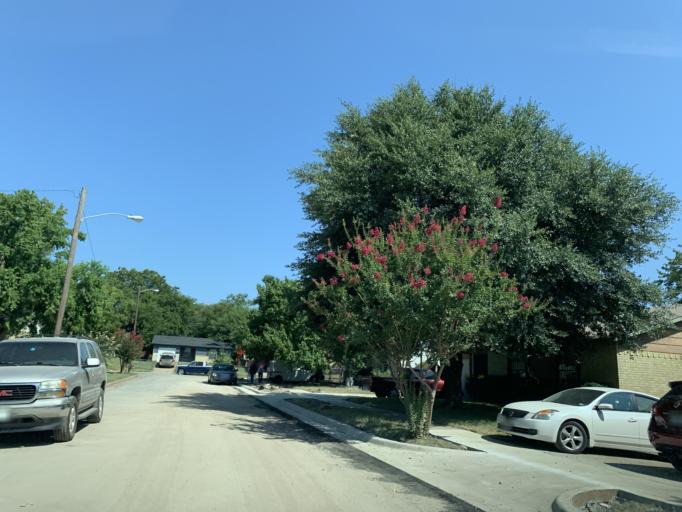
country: US
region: Texas
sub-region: Dallas County
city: Hutchins
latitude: 32.6592
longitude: -96.7572
